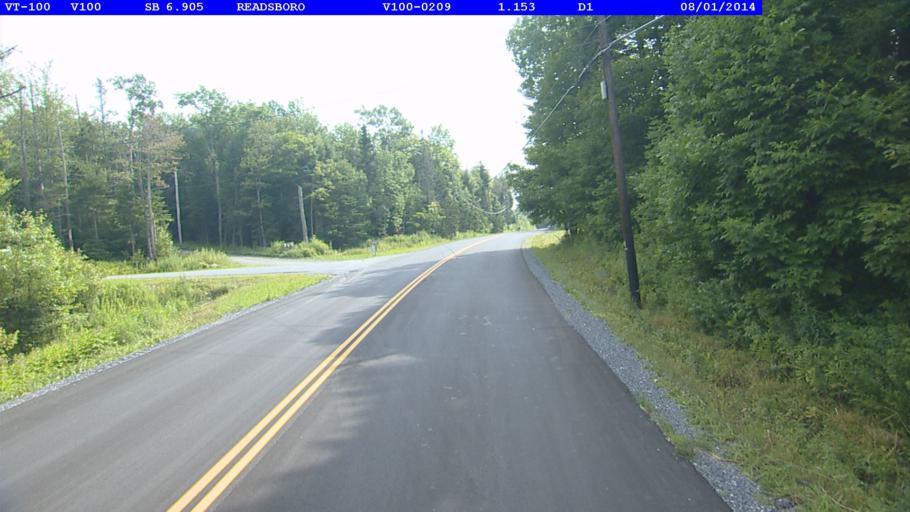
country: US
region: Massachusetts
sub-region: Berkshire County
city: North Adams
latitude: 42.8222
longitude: -73.0038
